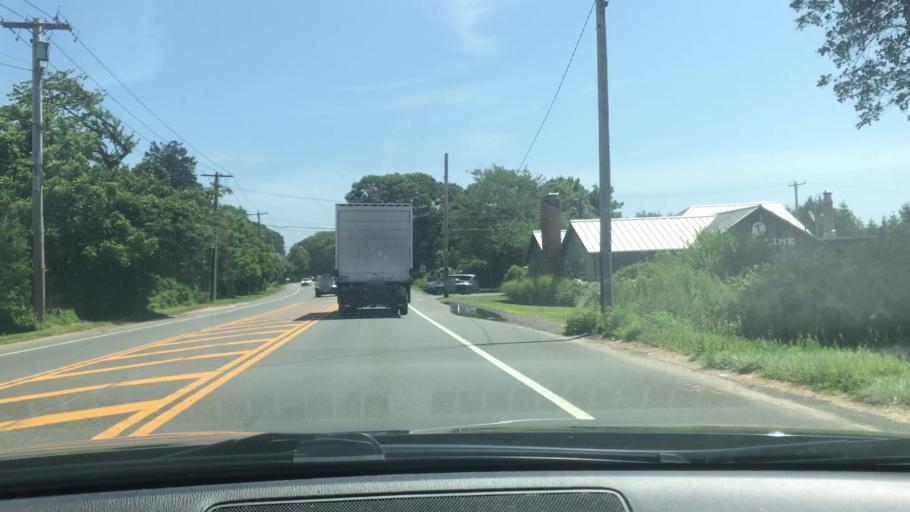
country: US
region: New York
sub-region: Suffolk County
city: Bridgehampton
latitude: 40.9447
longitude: -72.2635
